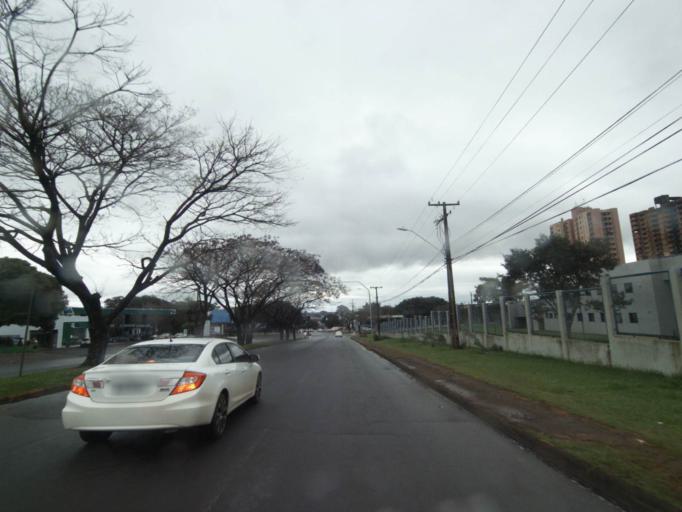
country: BR
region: Parana
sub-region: Foz Do Iguacu
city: Foz do Iguacu
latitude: -25.5172
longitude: -54.5734
